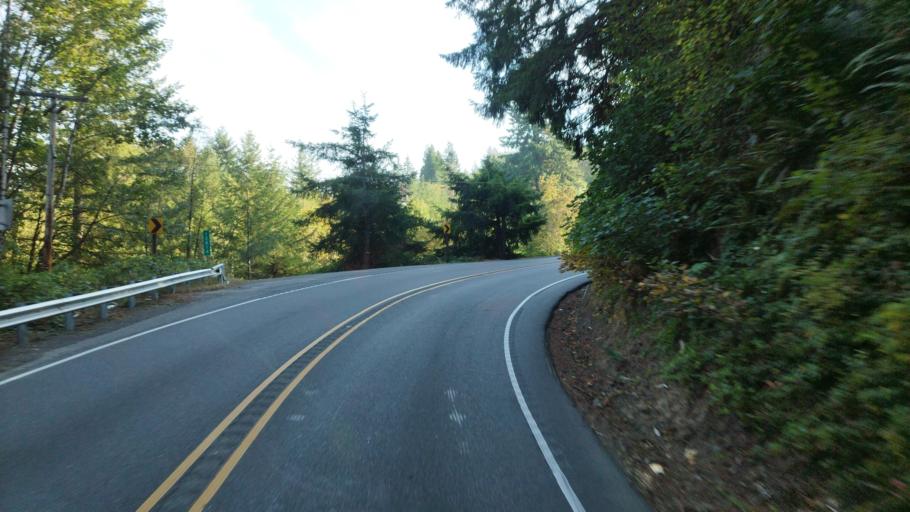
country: US
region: Oregon
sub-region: Washington County
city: Bethany
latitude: 45.6161
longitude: -122.8601
